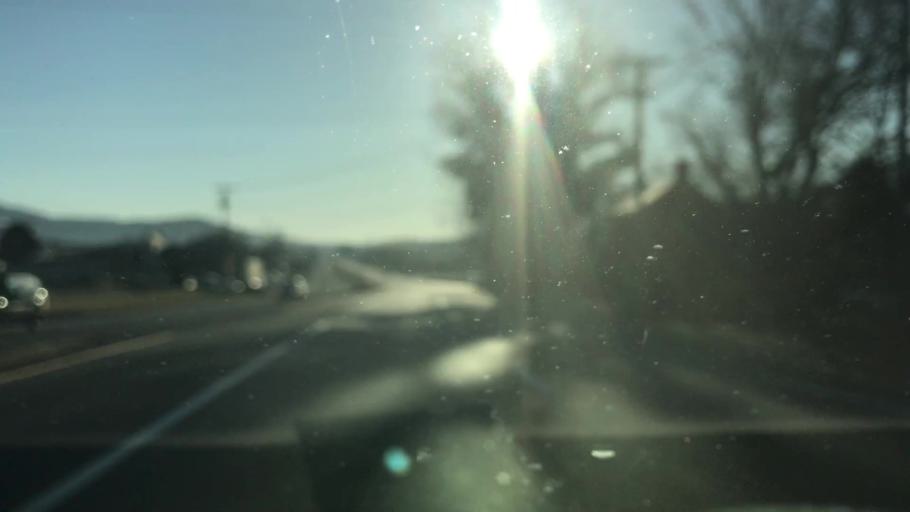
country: US
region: Virginia
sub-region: Botetourt County
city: Blue Ridge
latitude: 37.3869
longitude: -79.7378
